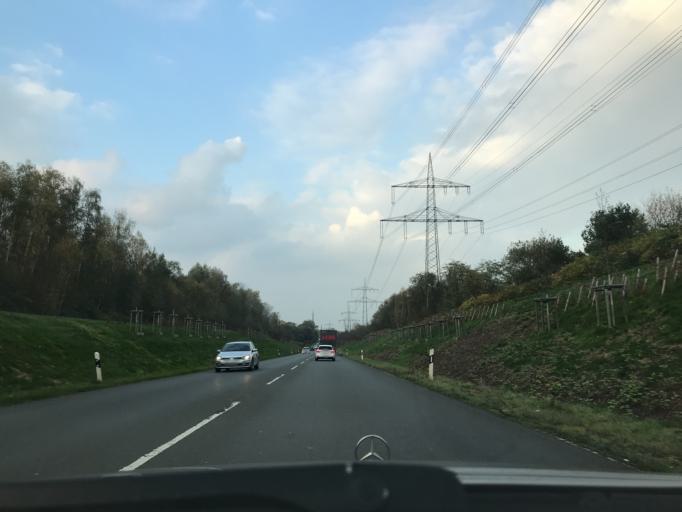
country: DE
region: North Rhine-Westphalia
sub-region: Regierungsbezirk Munster
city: Gelsenkirchen
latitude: 51.4862
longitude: 7.0983
